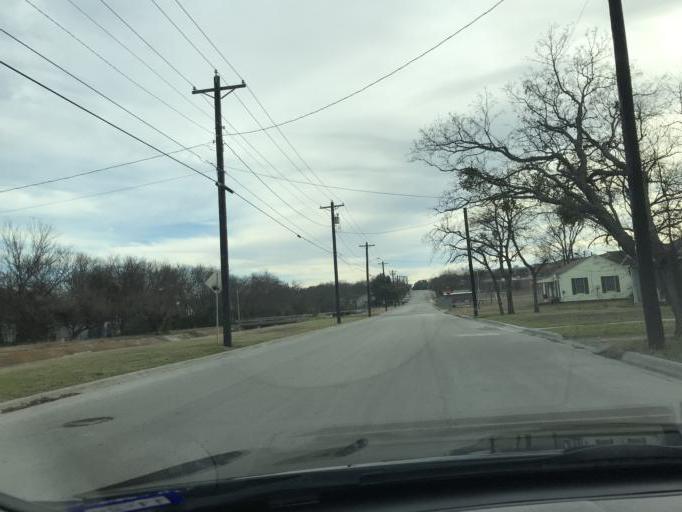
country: US
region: Texas
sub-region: Denton County
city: Denton
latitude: 33.2212
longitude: -97.1391
